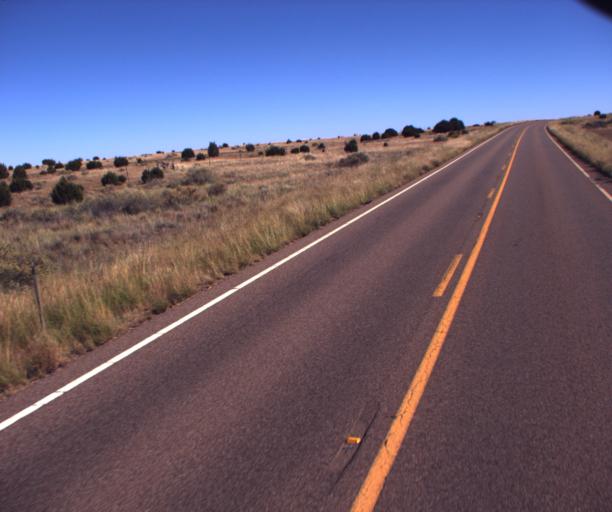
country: US
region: Arizona
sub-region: Navajo County
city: Heber-Overgaard
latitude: 34.4819
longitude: -110.3352
